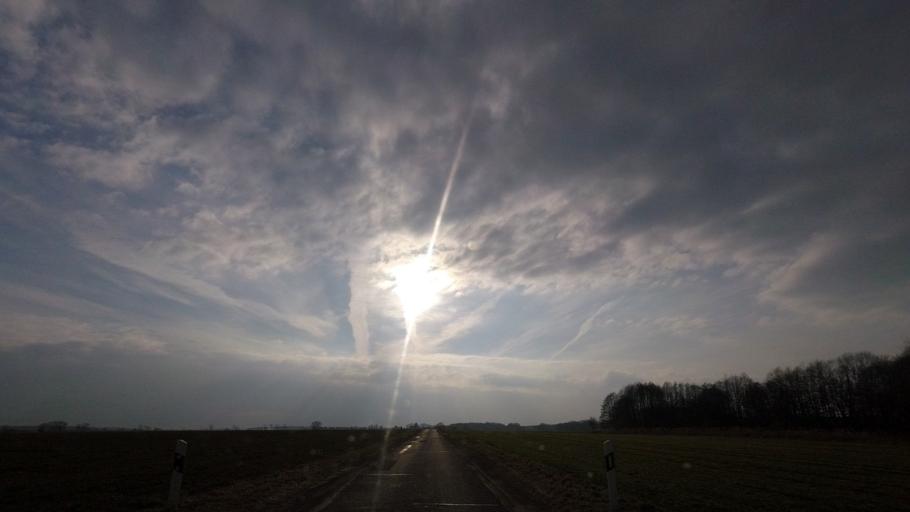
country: DE
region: Brandenburg
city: Belzig
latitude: 52.1568
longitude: 12.6691
